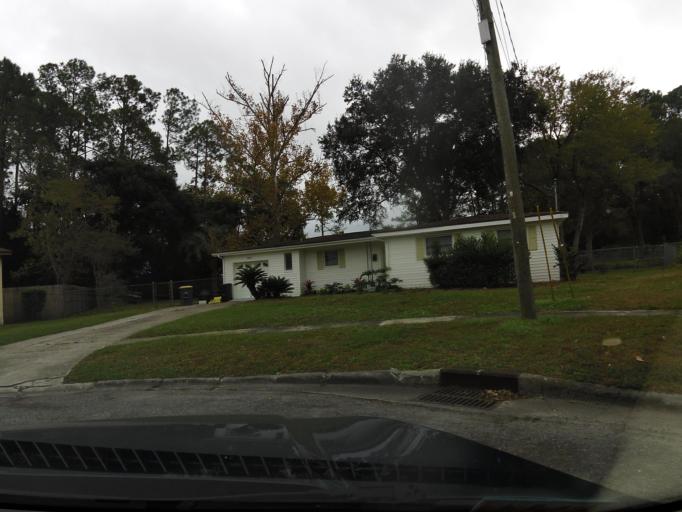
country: US
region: Florida
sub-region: Duval County
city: Jacksonville
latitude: 30.2742
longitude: -81.5992
